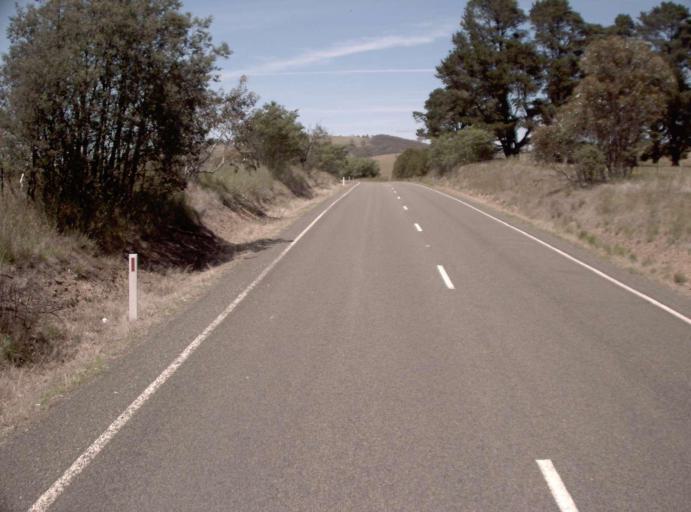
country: AU
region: Victoria
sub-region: Alpine
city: Mount Beauty
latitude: -37.1476
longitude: 147.6483
